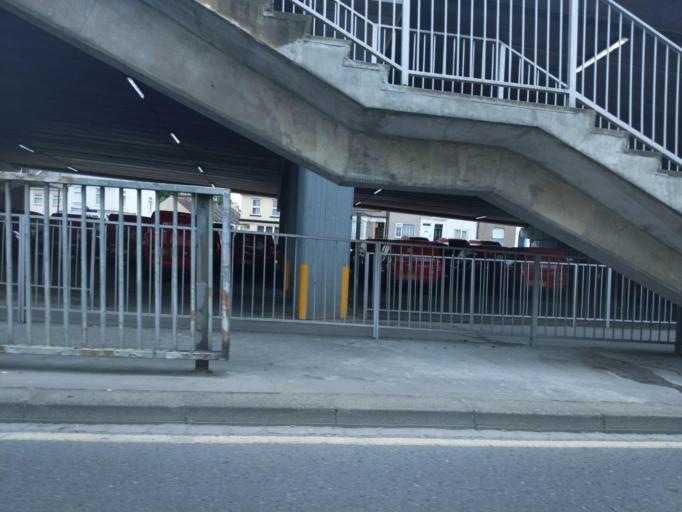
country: GB
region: England
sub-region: Greater London
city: Croydon
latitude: 51.3760
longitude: -0.1070
